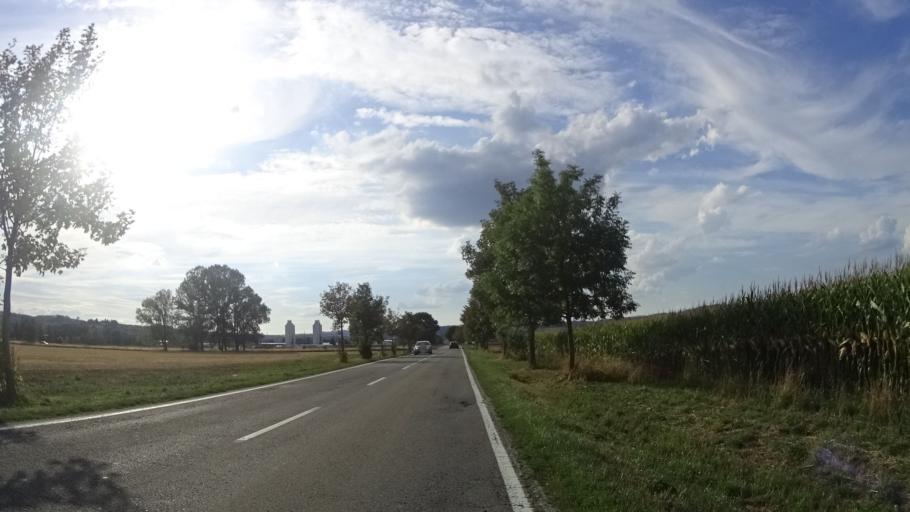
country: CZ
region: Olomoucky
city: Lestina
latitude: 49.8724
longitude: 16.9069
